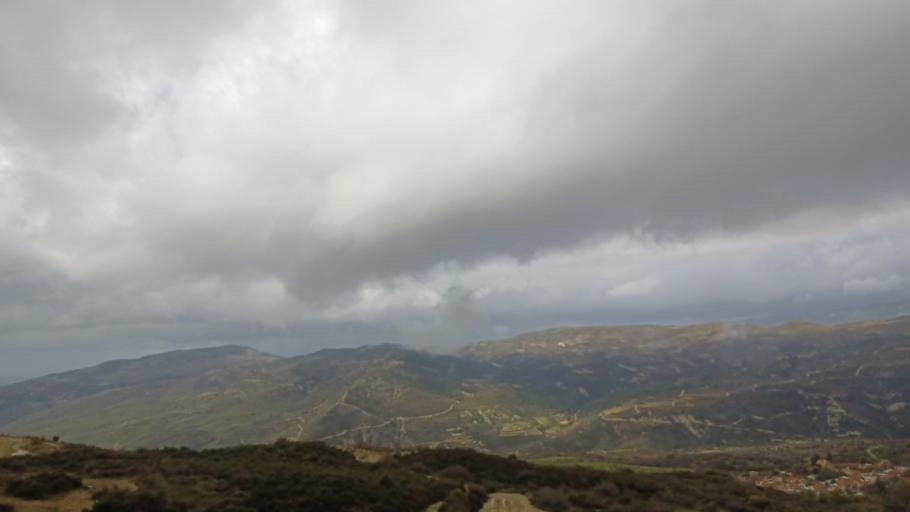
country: CY
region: Limassol
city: Pachna
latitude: 34.8327
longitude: 32.7439
